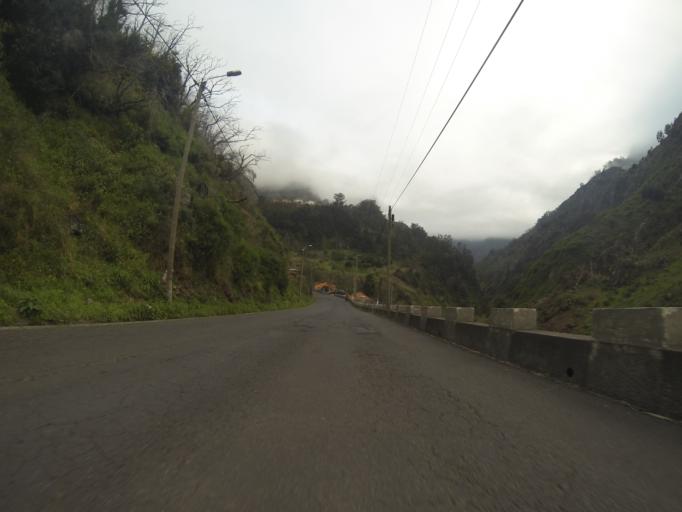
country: PT
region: Madeira
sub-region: Camara de Lobos
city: Curral das Freiras
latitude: 32.7241
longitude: -16.9666
